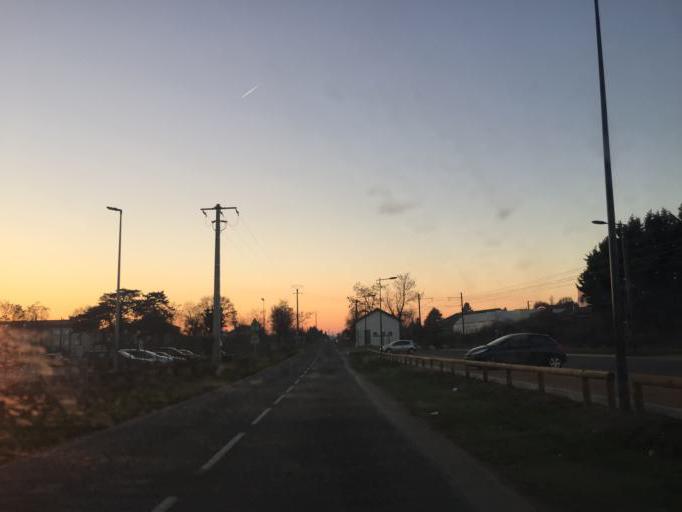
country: FR
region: Rhone-Alpes
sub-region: Departement de l'Ain
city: Beligneux
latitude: 45.8485
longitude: 5.1234
